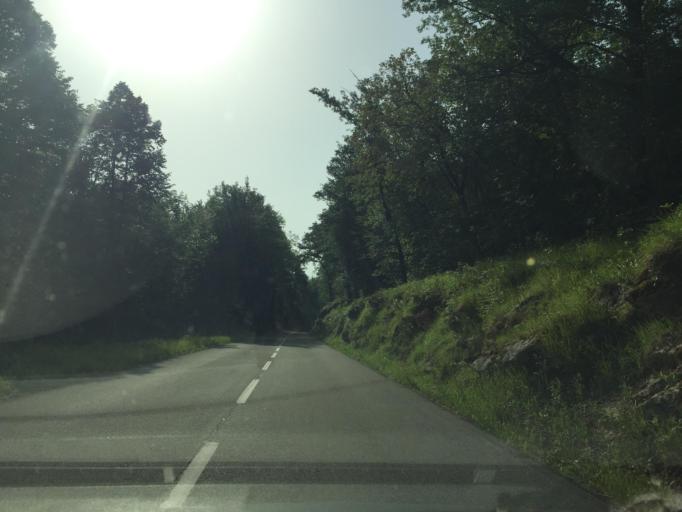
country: HR
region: Primorsko-Goranska
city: Matulji
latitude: 45.4059
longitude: 14.2752
